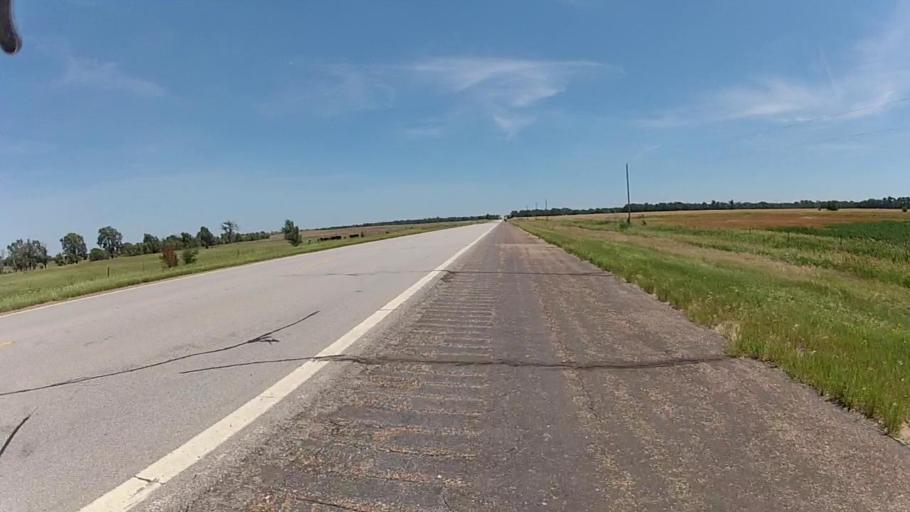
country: US
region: Kansas
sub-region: Barber County
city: Medicine Lodge
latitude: 37.2533
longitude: -98.3146
